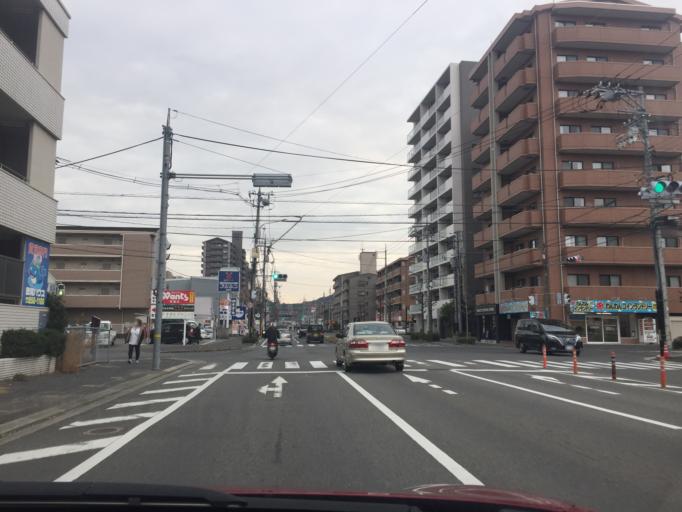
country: JP
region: Hiroshima
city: Hiroshima-shi
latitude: 34.4426
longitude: 132.4585
